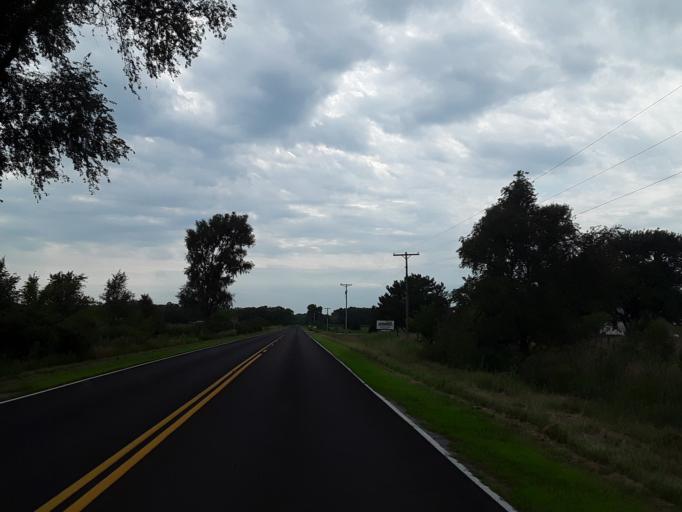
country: US
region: Nebraska
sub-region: Saunders County
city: Yutan
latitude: 41.2193
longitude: -96.3317
